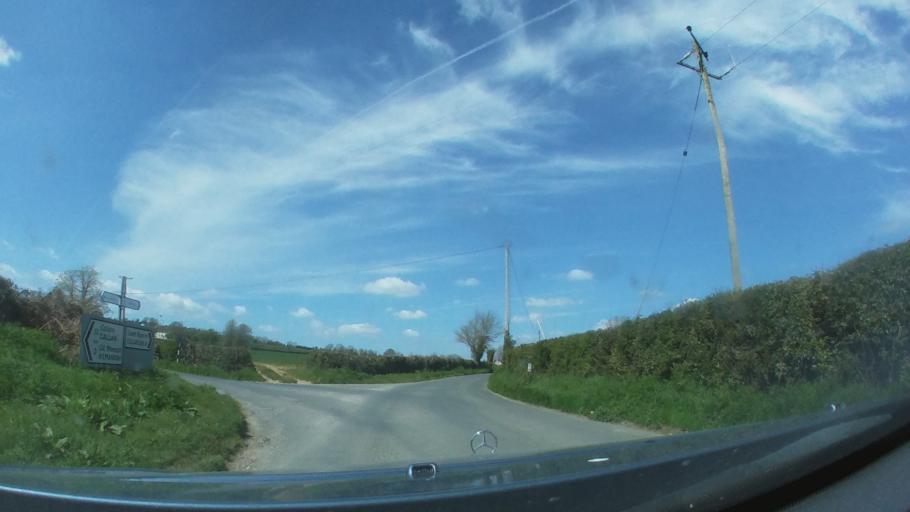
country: IE
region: Leinster
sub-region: Kilkenny
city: Callan
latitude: 52.6238
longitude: -7.4326
